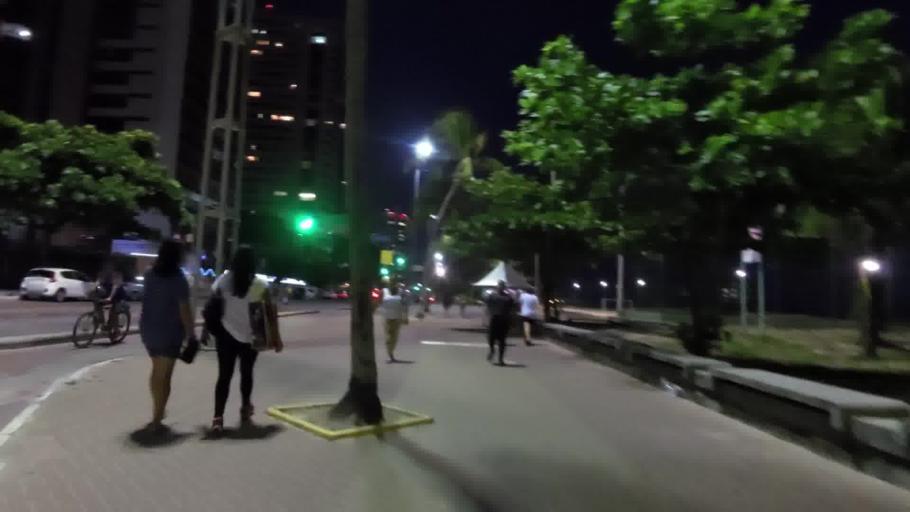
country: BR
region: Pernambuco
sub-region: Recife
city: Recife
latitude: -8.0946
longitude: -34.8827
